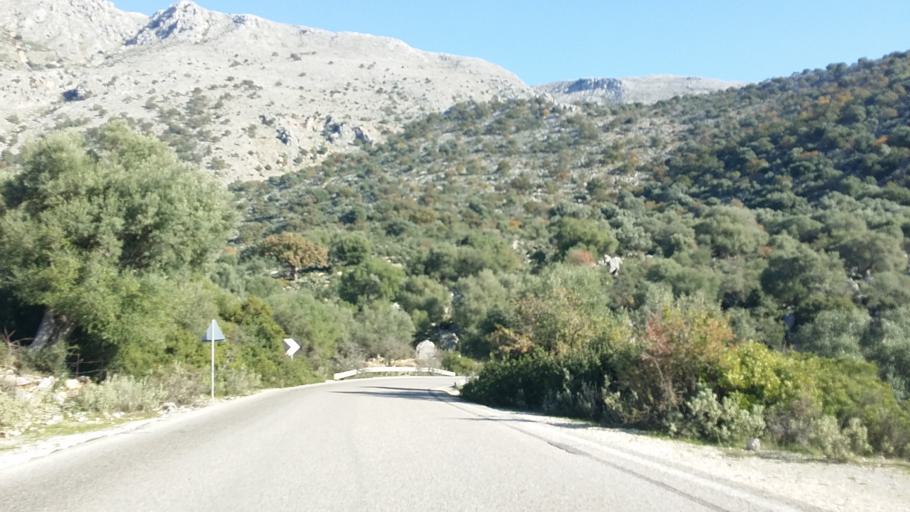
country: GR
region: West Greece
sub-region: Nomos Aitolias kai Akarnanias
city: Kandila
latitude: 38.7198
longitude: 20.8960
